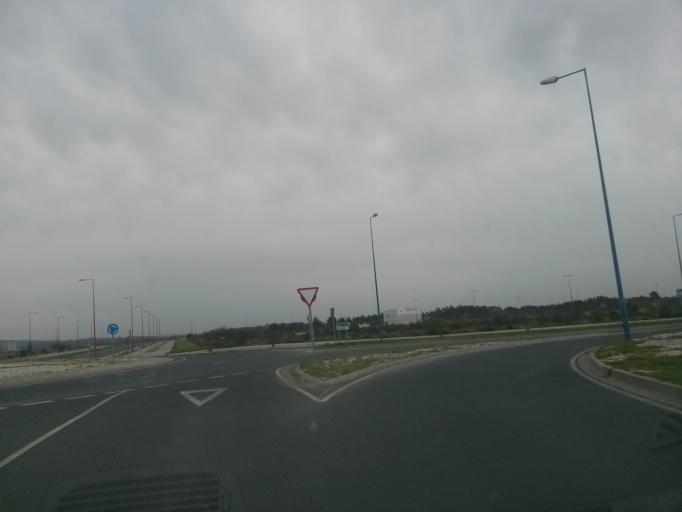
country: ES
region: Galicia
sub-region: Provincia de Lugo
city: Lugo
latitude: 43.0424
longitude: -7.5539
